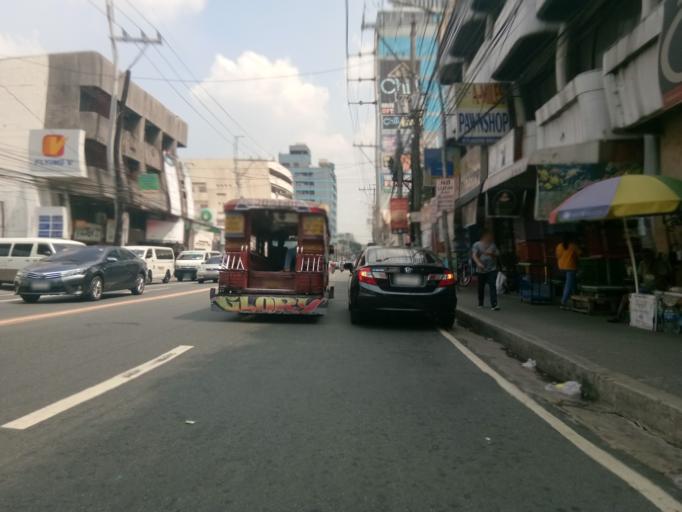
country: PH
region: Metro Manila
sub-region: Quezon City
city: Quezon City
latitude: 14.6201
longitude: 121.0595
